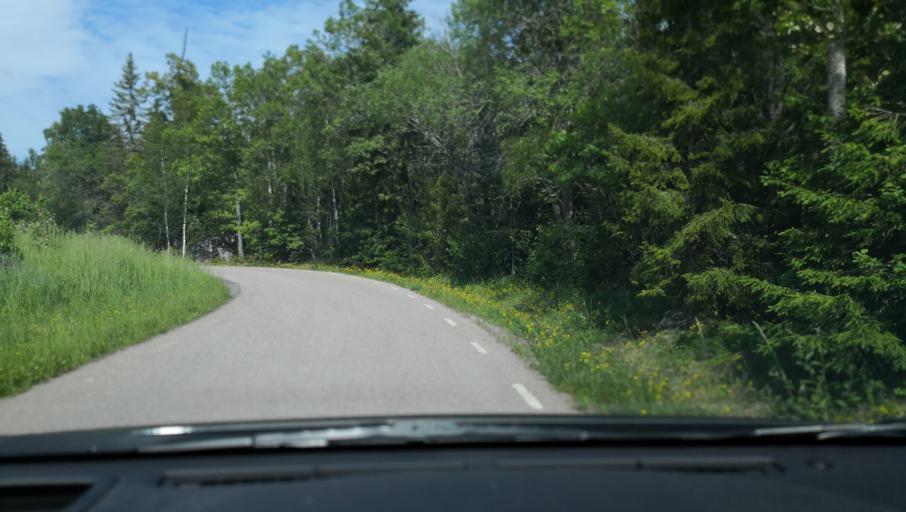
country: SE
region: Uppsala
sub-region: Uppsala Kommun
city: Alsike
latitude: 59.7028
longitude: 17.6509
